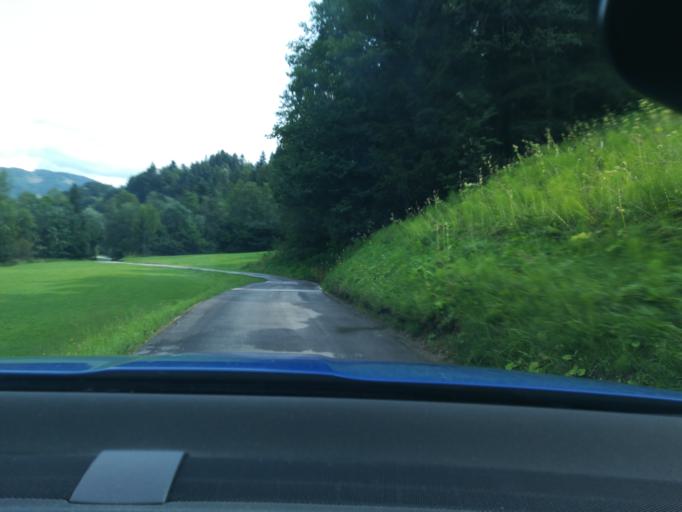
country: AT
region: Salzburg
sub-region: Politischer Bezirk Hallein
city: Abtenau
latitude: 47.5762
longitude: 13.3730
